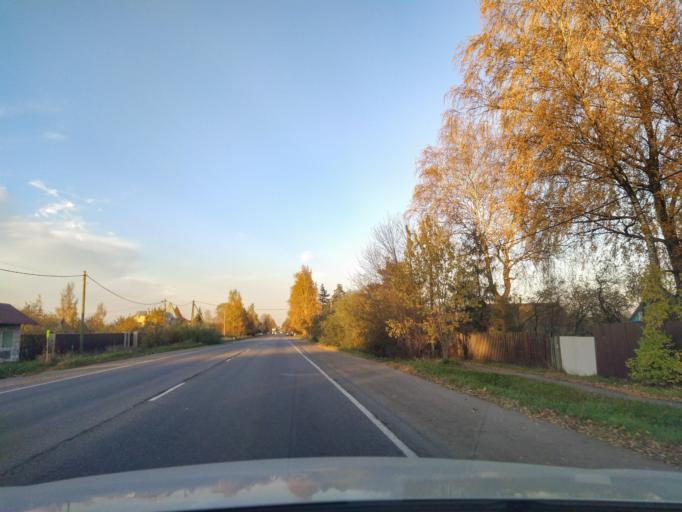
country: RU
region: Leningrad
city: Maloye Verevo
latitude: 59.6127
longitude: 30.2008
